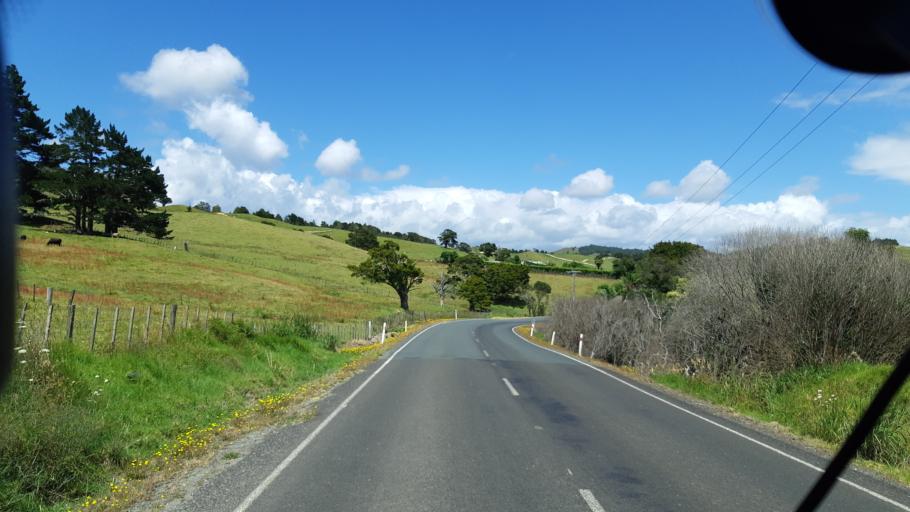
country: NZ
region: Northland
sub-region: Far North District
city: Taipa
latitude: -35.2687
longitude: 173.4951
